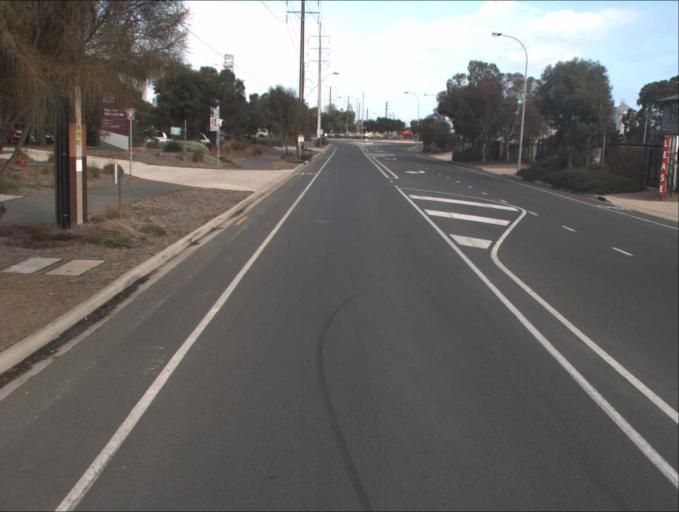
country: AU
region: South Australia
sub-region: Port Adelaide Enfield
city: Birkenhead
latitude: -34.7883
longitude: 138.5065
